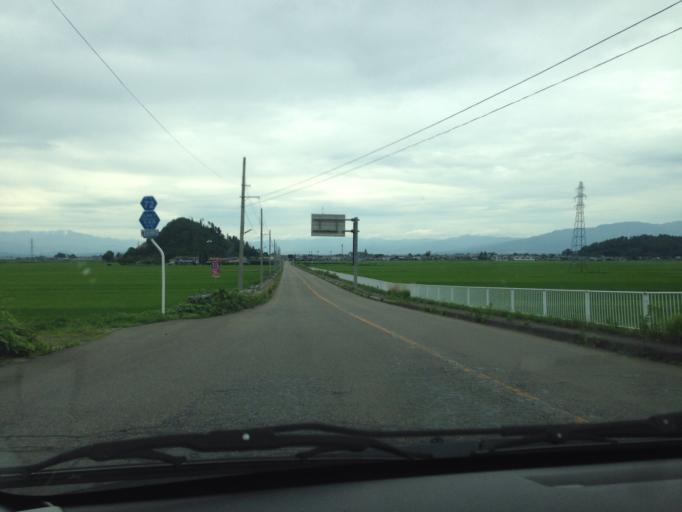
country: JP
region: Fukushima
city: Kitakata
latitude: 37.4360
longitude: 139.8812
